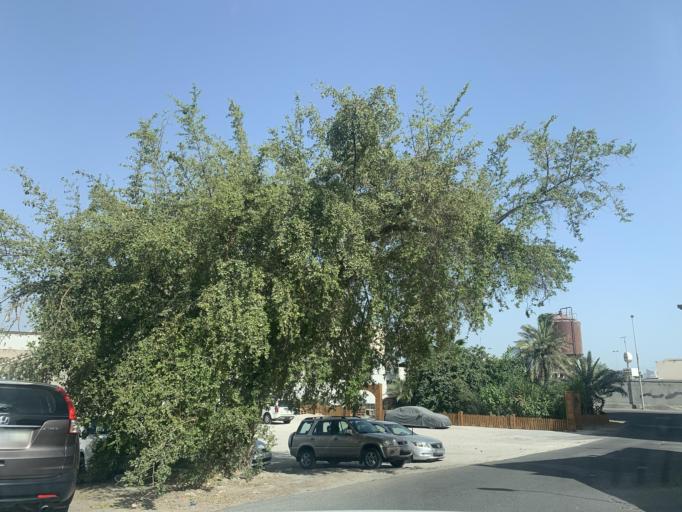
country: BH
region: Manama
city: Jidd Hafs
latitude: 26.2083
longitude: 50.5553
